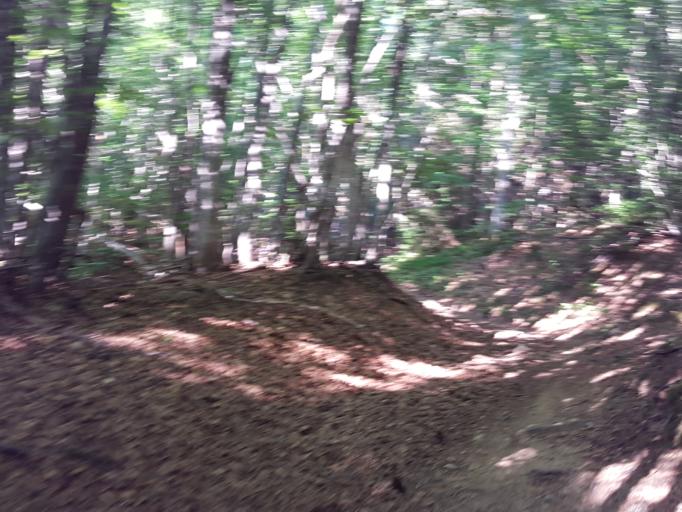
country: IT
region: Tuscany
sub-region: Provincia di Pistoia
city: Abetone
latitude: 44.1556
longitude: 10.6762
